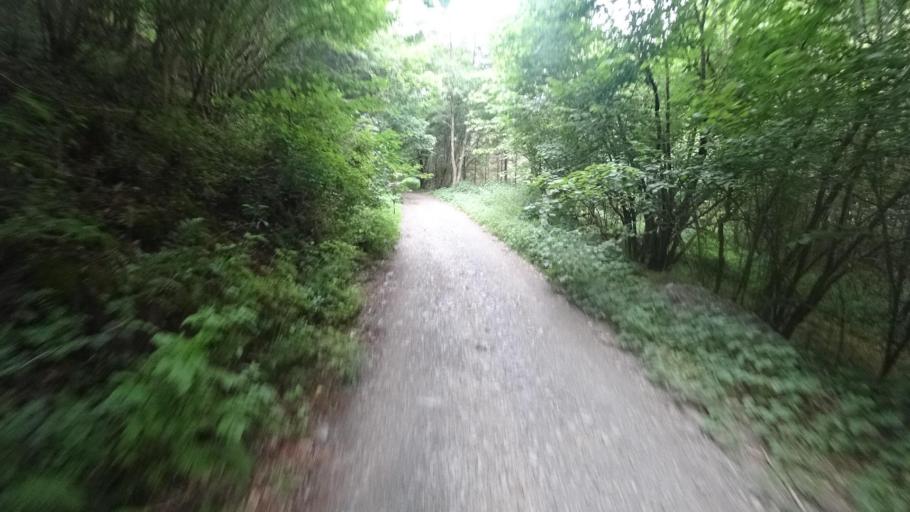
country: DE
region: Rheinland-Pfalz
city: Kesseling
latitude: 50.4833
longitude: 7.0108
